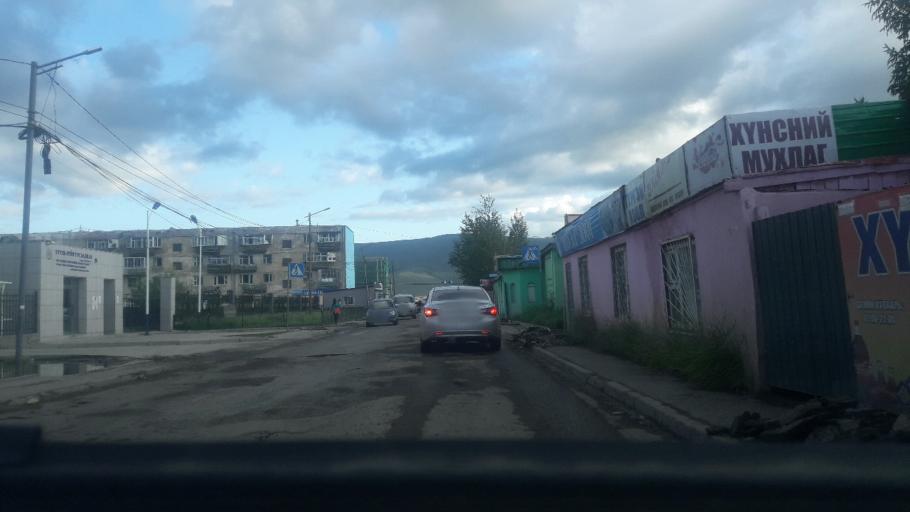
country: MN
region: Ulaanbaatar
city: Ulaanbaatar
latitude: 47.9146
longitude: 106.9946
